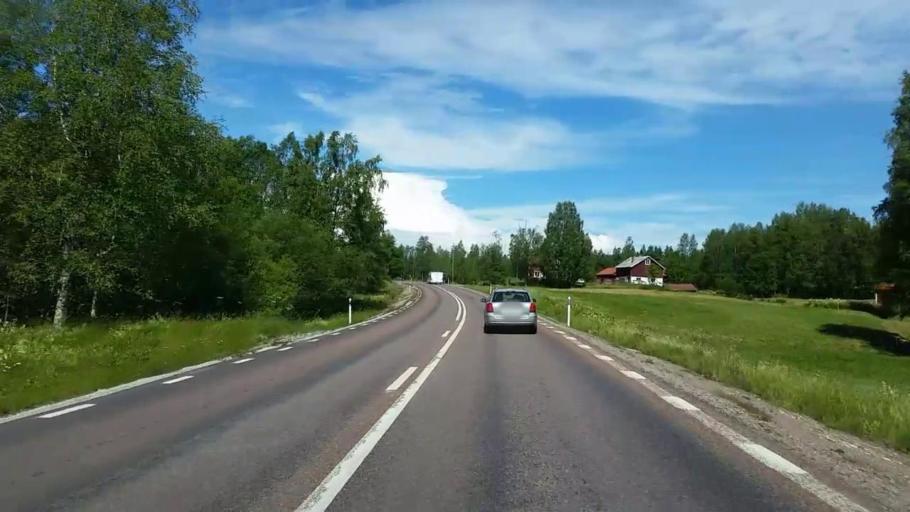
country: SE
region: Dalarna
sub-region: Rattviks Kommun
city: Raettvik
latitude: 60.9773
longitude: 15.2248
